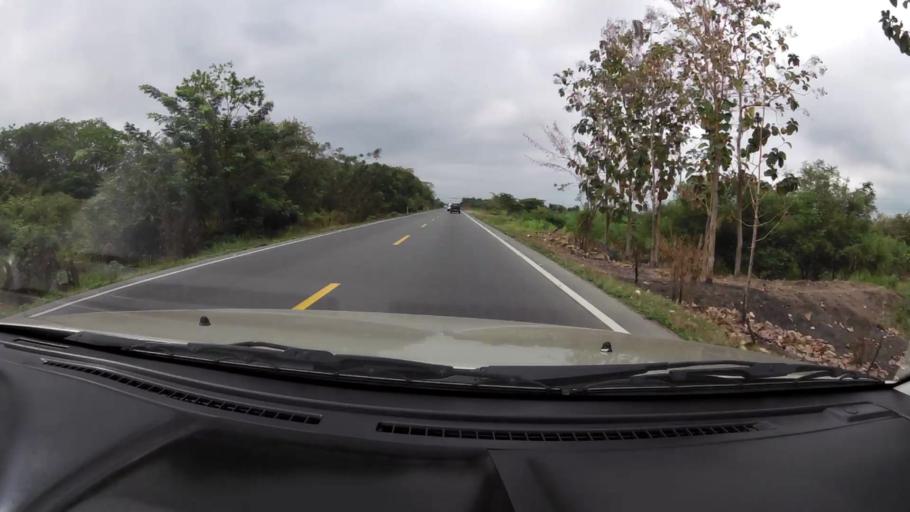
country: EC
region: Guayas
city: Naranjal
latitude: -2.4215
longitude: -79.6249
